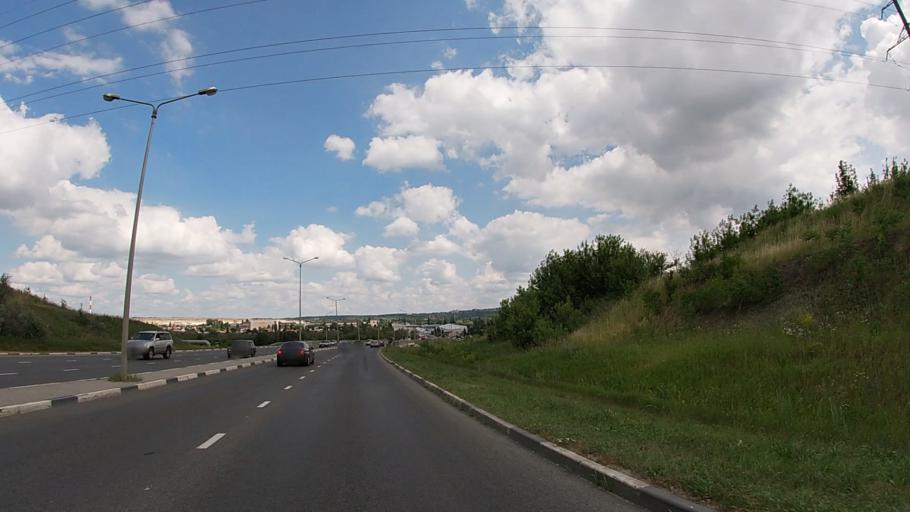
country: RU
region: Belgorod
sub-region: Belgorodskiy Rayon
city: Belgorod
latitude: 50.6048
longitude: 36.5303
